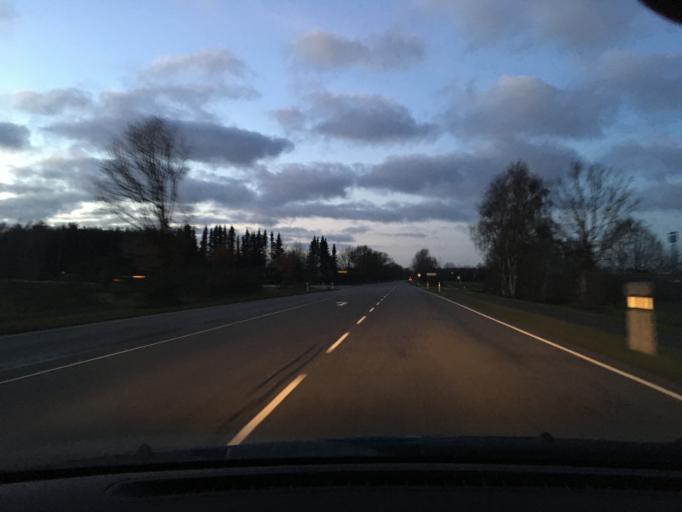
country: DE
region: Schleswig-Holstein
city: Ottenbuttel
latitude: 53.9866
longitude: 9.4968
